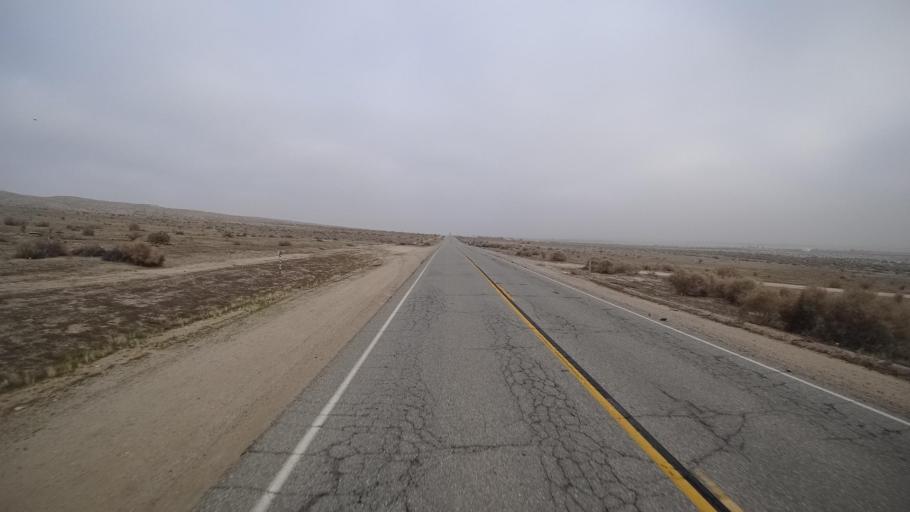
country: US
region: California
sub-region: Kern County
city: South Taft
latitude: 35.1301
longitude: -119.3849
